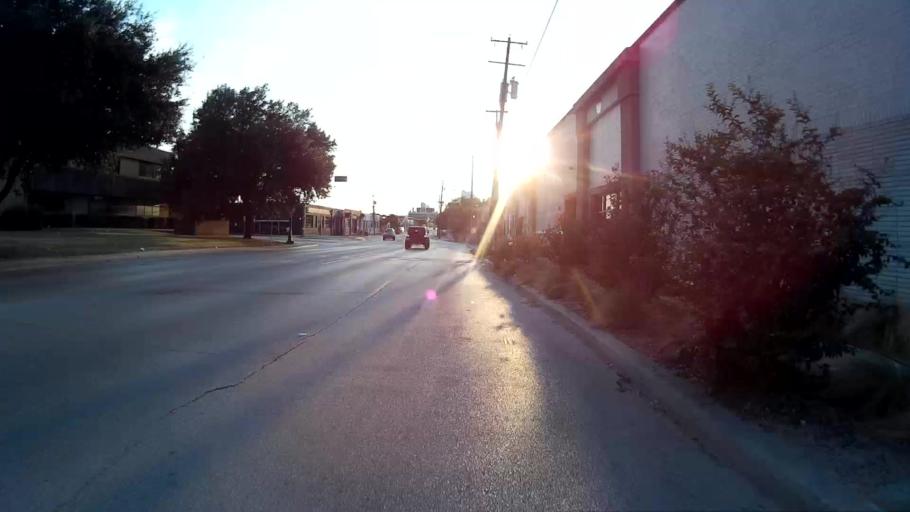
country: US
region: Texas
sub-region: Dallas County
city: Dallas
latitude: 32.7834
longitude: -96.7778
